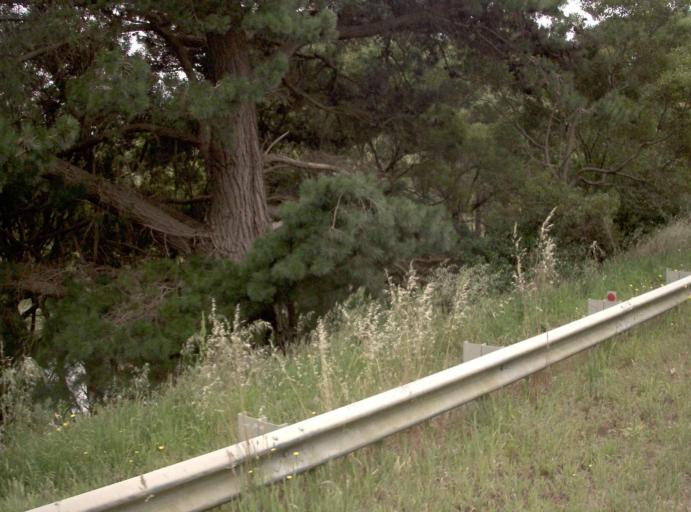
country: AU
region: Victoria
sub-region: Latrobe
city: Morwell
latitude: -38.6359
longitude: 146.1985
